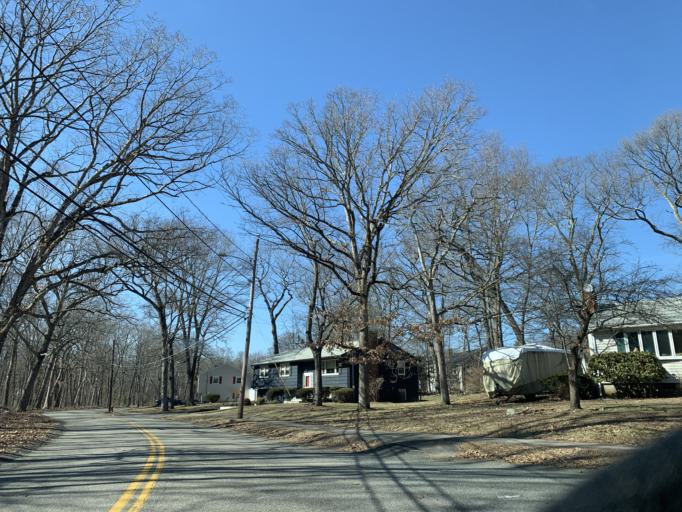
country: US
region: Massachusetts
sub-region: Norfolk County
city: Norwood
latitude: 42.1880
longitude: -71.2213
